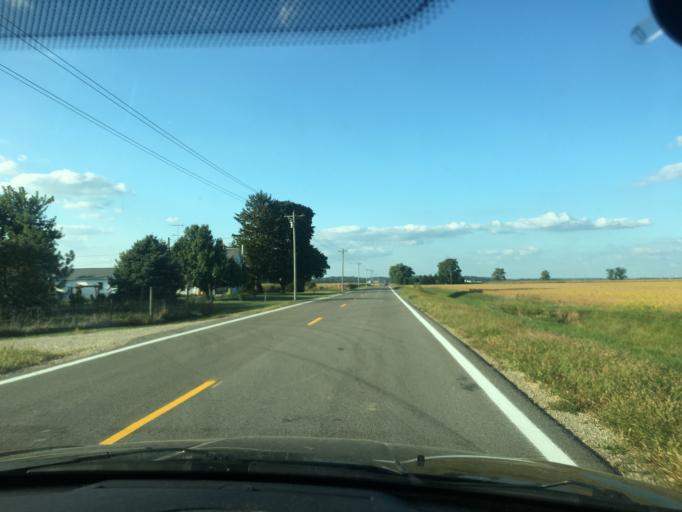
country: US
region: Ohio
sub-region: Logan County
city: West Liberty
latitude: 40.1894
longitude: -83.7815
